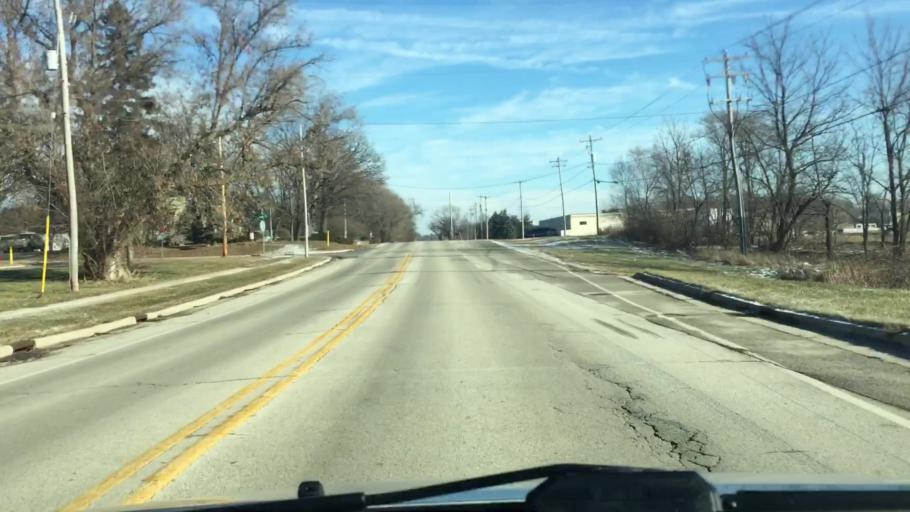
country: US
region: Wisconsin
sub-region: Waukesha County
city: Mukwonago
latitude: 42.8671
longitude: -88.3263
